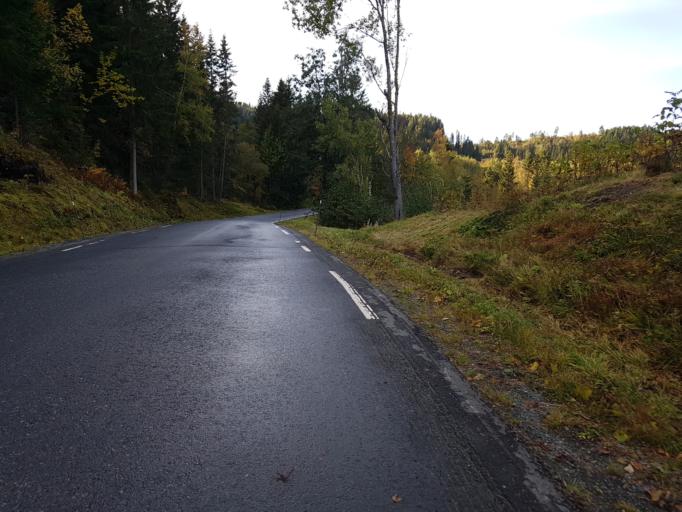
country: NO
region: Sor-Trondelag
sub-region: Klaebu
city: Klaebu
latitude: 63.3443
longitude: 10.5486
